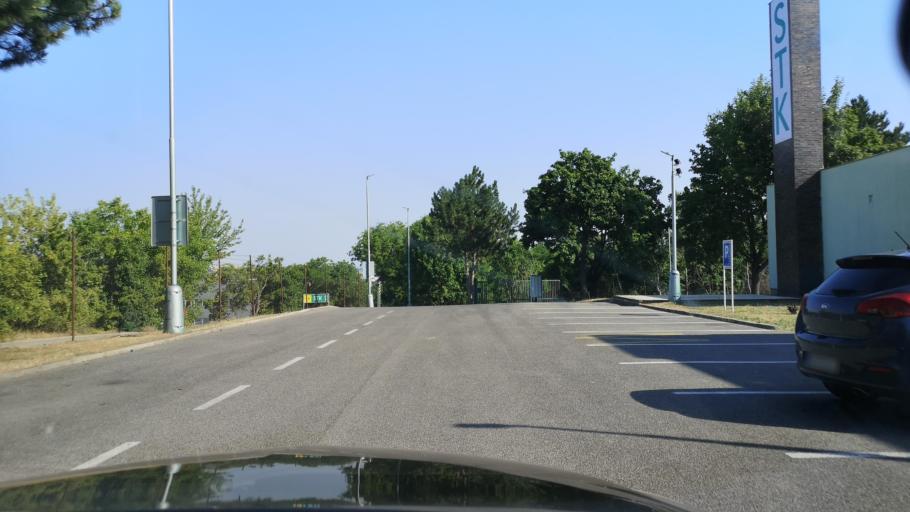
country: SK
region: Nitriansky
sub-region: Okres Nitra
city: Nitra
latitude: 48.3154
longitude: 18.0432
